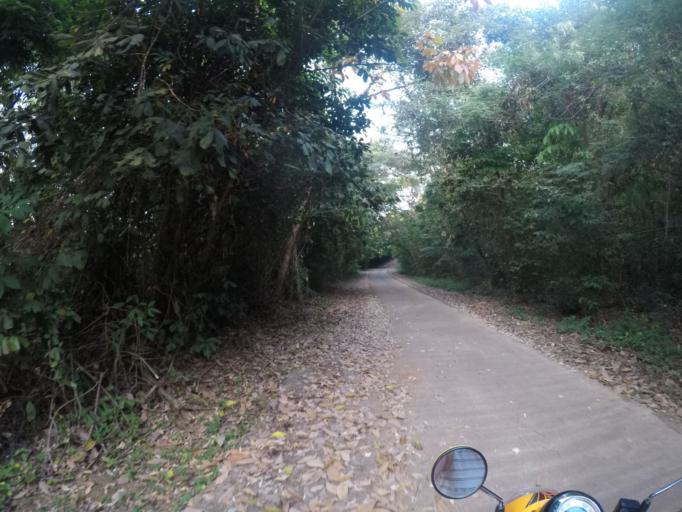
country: TH
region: Trat
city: Ko Kut
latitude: 11.8011
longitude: 102.4834
